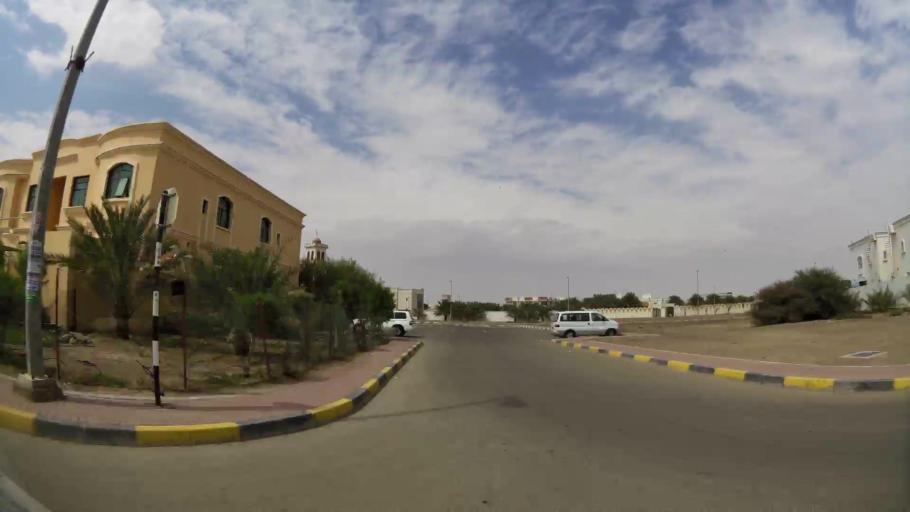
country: AE
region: Abu Dhabi
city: Al Ain
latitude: 24.1982
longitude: 55.7923
